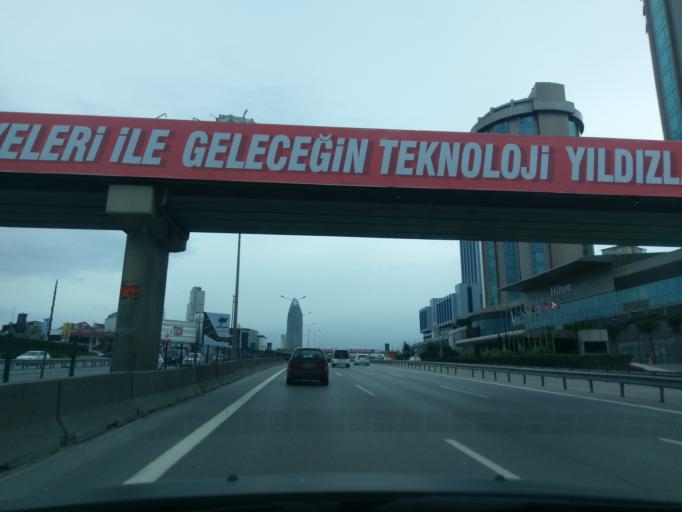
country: TR
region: Istanbul
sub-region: Atasehir
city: Atasehir
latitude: 40.9880
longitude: 29.0853
